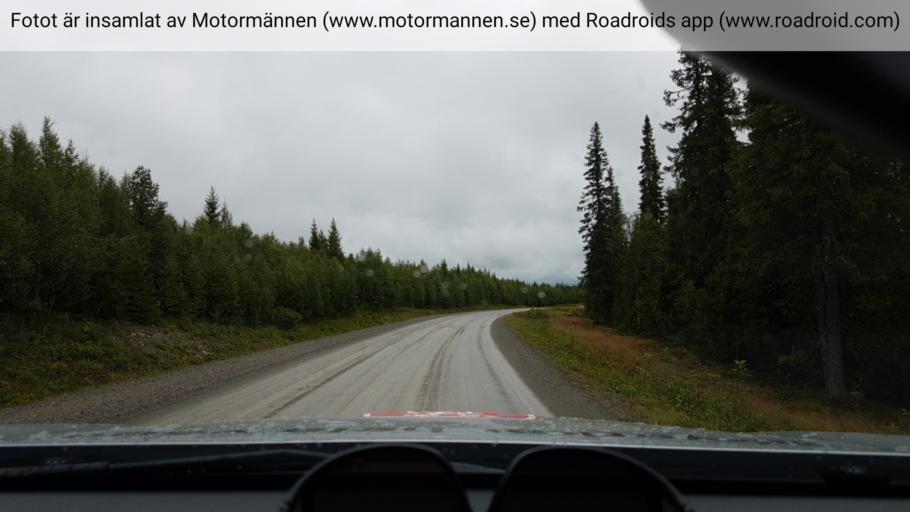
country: SE
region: Vaesterbotten
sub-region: Storumans Kommun
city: Storuman
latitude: 64.9154
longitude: 17.2704
